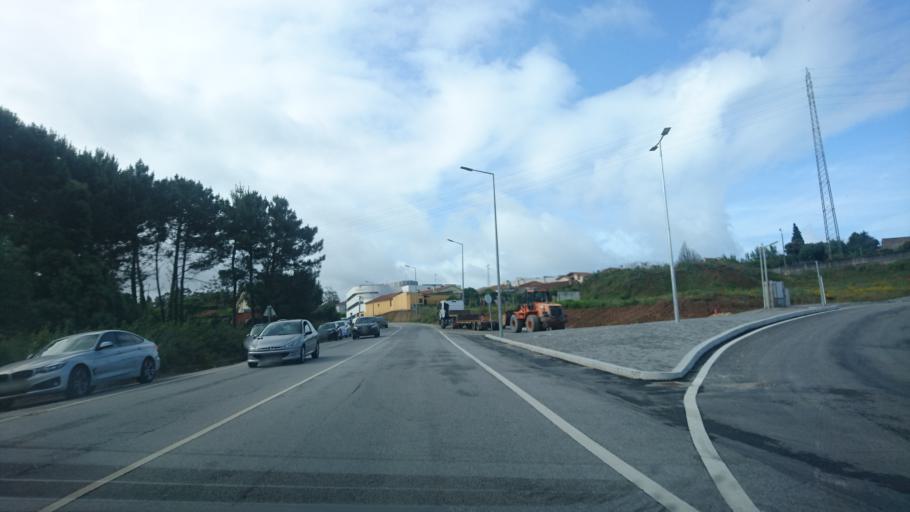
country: PT
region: Aveiro
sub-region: Espinho
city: Silvalde
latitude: 41.0075
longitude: -8.6213
